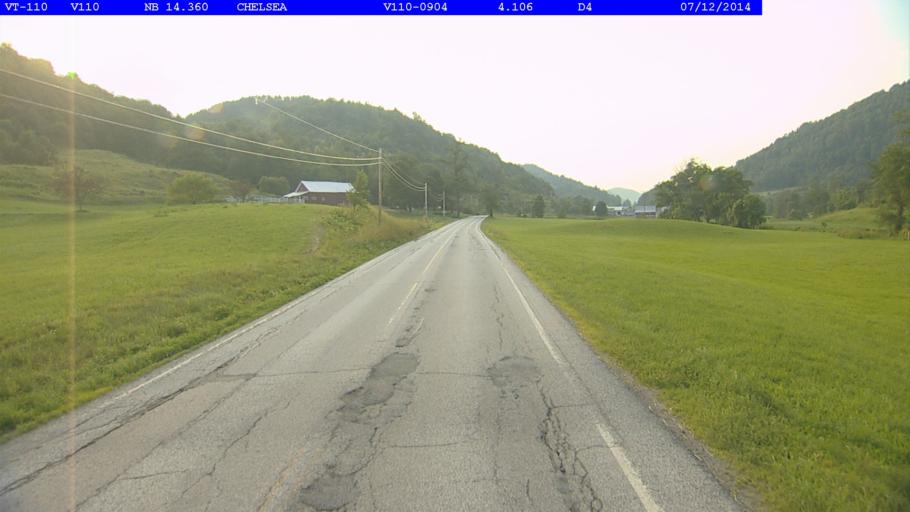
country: US
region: Vermont
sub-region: Orange County
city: Chelsea
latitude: 44.0027
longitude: -72.4564
